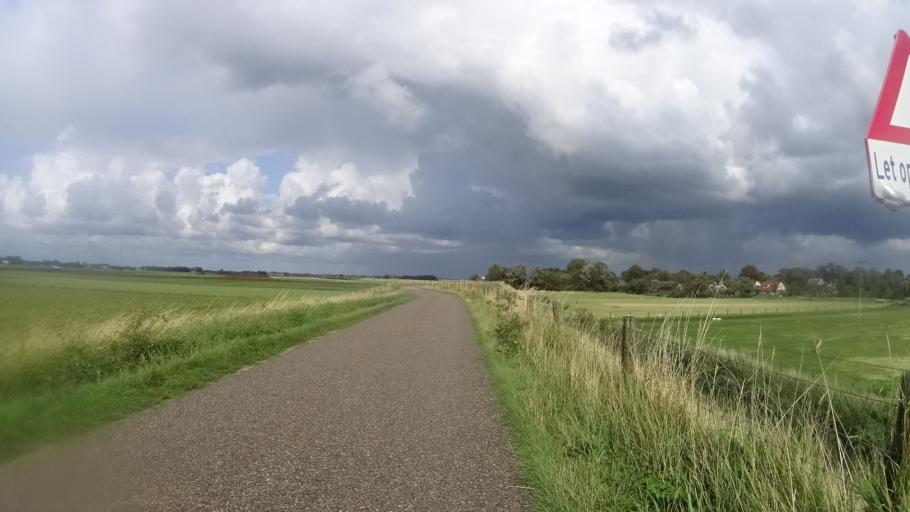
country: NL
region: North Holland
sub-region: Gemeente Schagen
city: Harenkarspel
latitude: 52.7719
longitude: 4.7369
